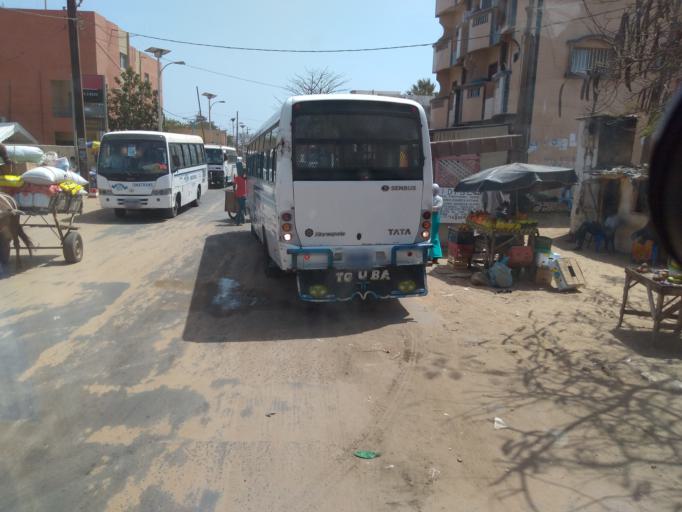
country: SN
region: Dakar
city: Pikine
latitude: 14.7670
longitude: -17.3675
